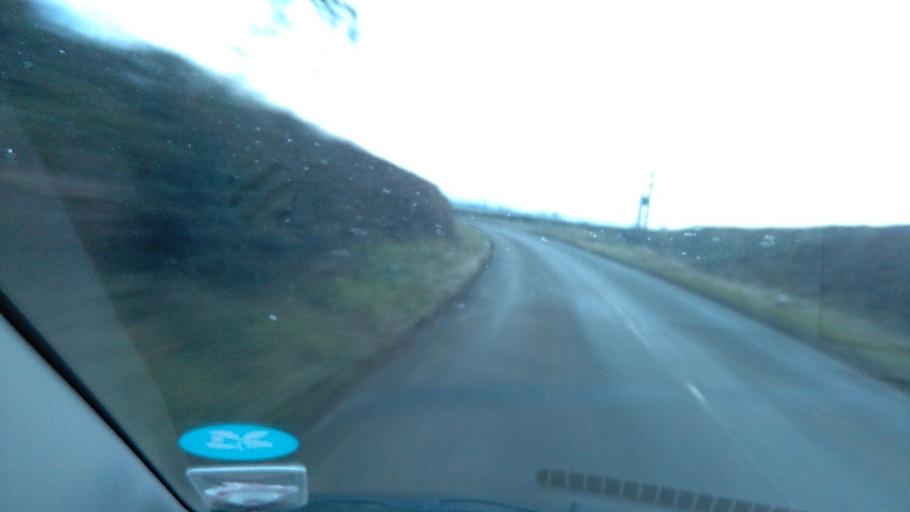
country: GB
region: England
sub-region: Leicestershire
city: Melton Mowbray
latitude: 52.7934
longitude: -0.8893
